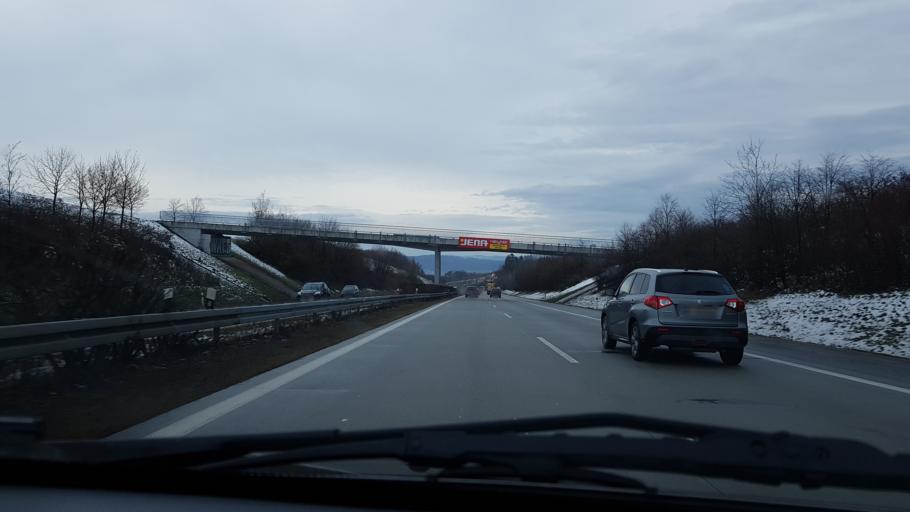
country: CZ
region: Olomoucky
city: Dolni Ujezd
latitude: 49.5557
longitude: 17.5242
